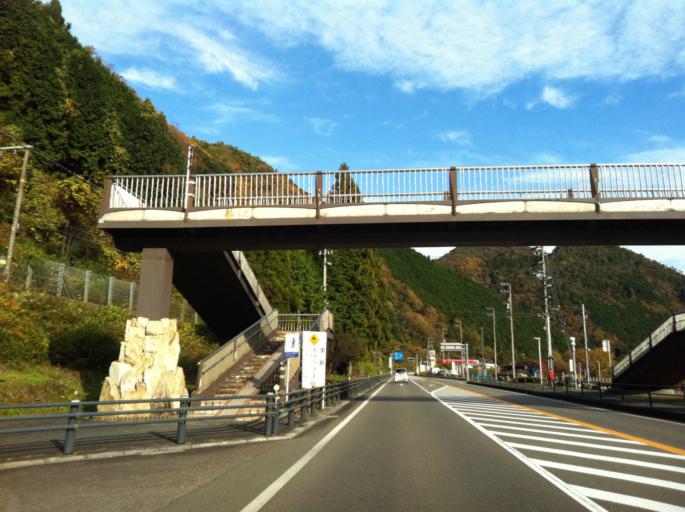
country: JP
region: Gifu
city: Minokamo
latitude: 35.5340
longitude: 137.1140
